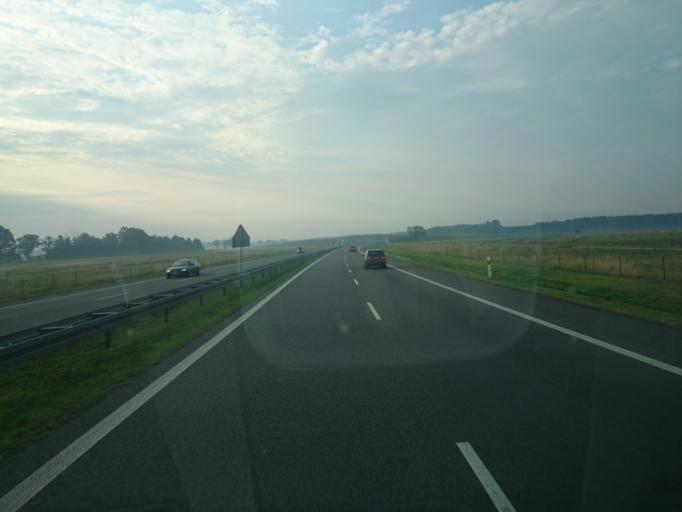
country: PL
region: West Pomeranian Voivodeship
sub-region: Powiat pyrzycki
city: Lipiany
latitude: 52.9454
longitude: 14.9665
